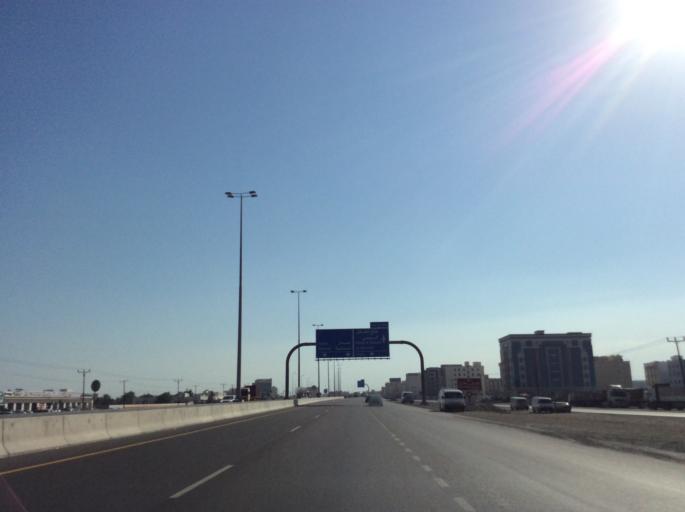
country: OM
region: Al Batinah
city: Al Liwa'
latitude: 24.4395
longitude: 56.6076
